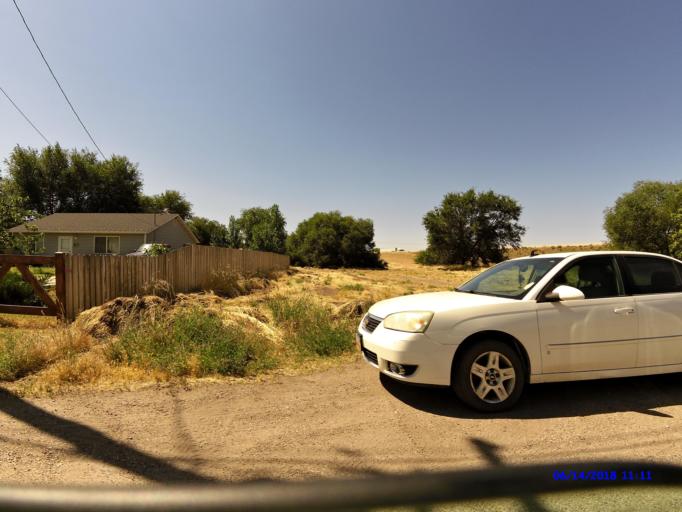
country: US
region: Utah
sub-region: Weber County
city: Ogden
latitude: 41.2194
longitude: -112.0024
